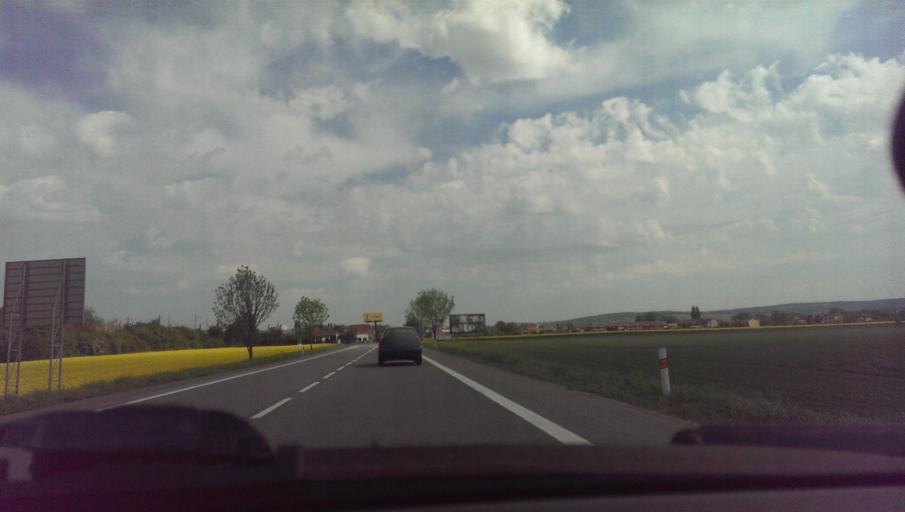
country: CZ
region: Zlin
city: Babice
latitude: 49.1322
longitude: 17.4856
